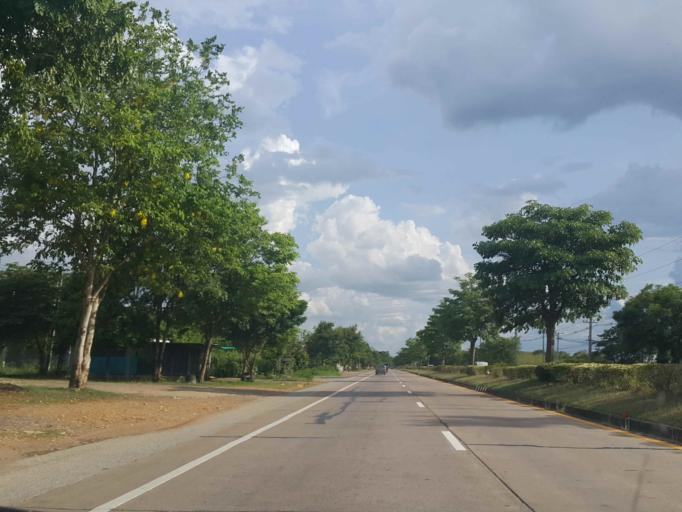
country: TH
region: Phrae
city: Sung Men
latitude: 18.0209
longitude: 100.1096
